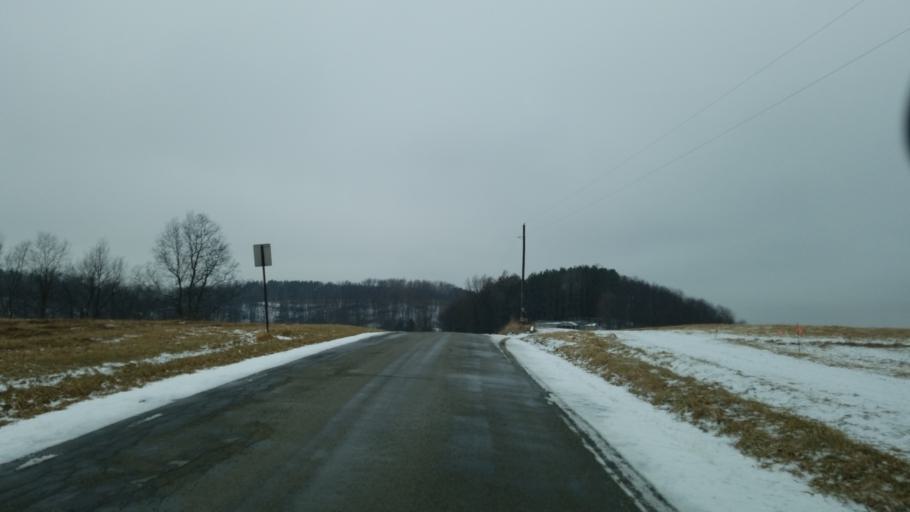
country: US
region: Pennsylvania
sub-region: Jefferson County
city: Sykesville
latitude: 41.0840
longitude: -78.8220
